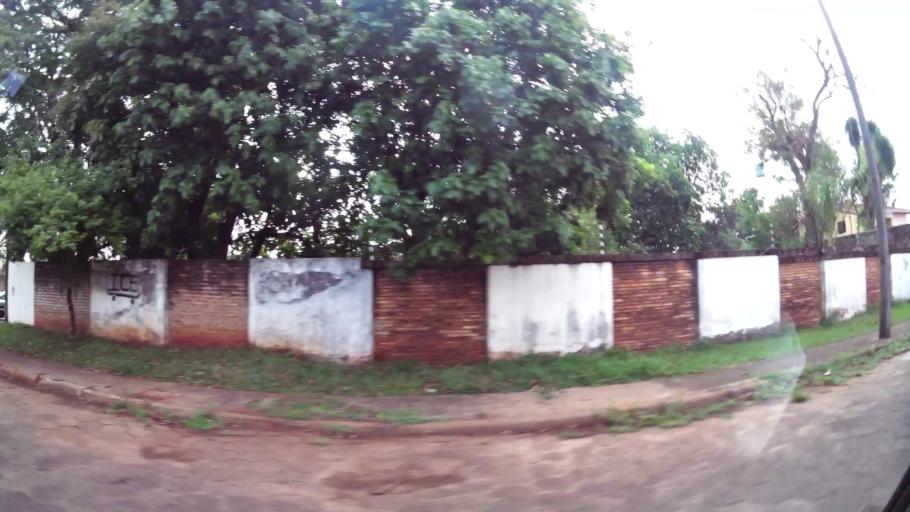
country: PY
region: Alto Parana
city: Presidente Franco
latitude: -25.5268
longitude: -54.6331
